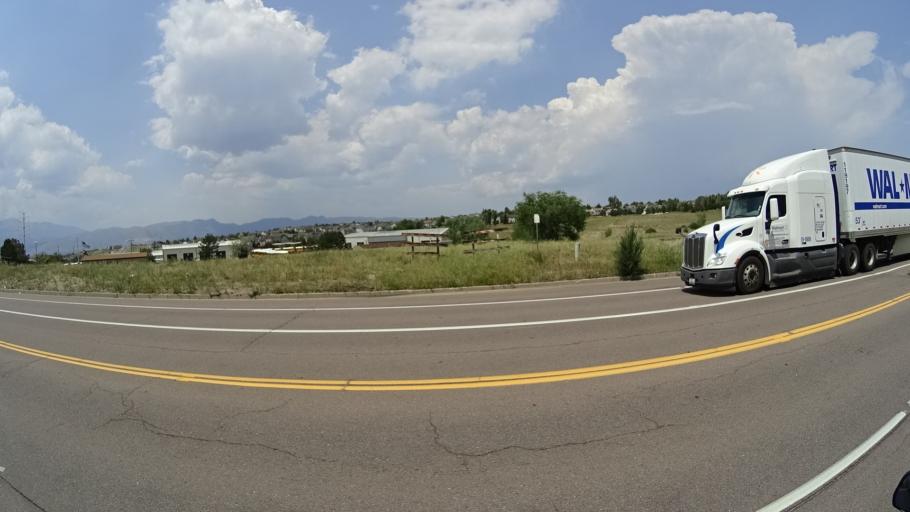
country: US
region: Colorado
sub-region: El Paso County
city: Black Forest
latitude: 38.9413
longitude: -104.7289
